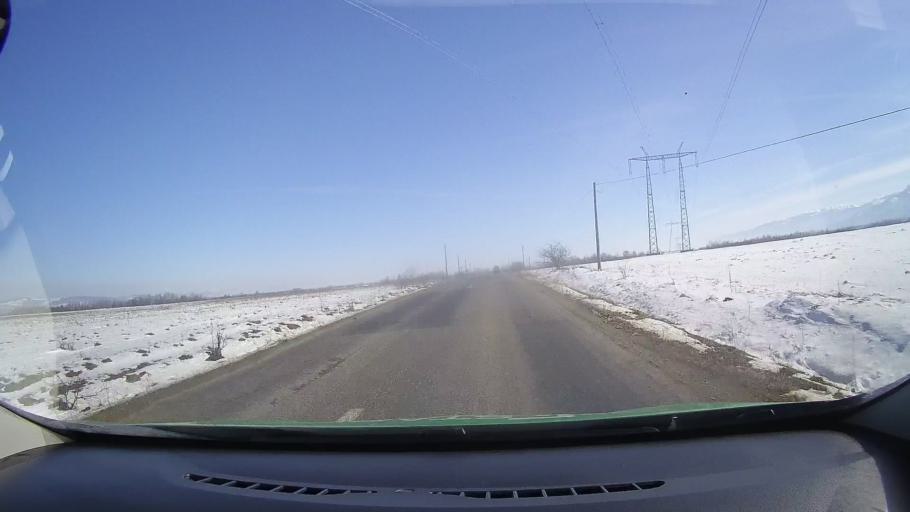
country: RO
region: Brasov
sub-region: Oras Victoria
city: Victoria
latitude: 45.7339
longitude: 24.7273
